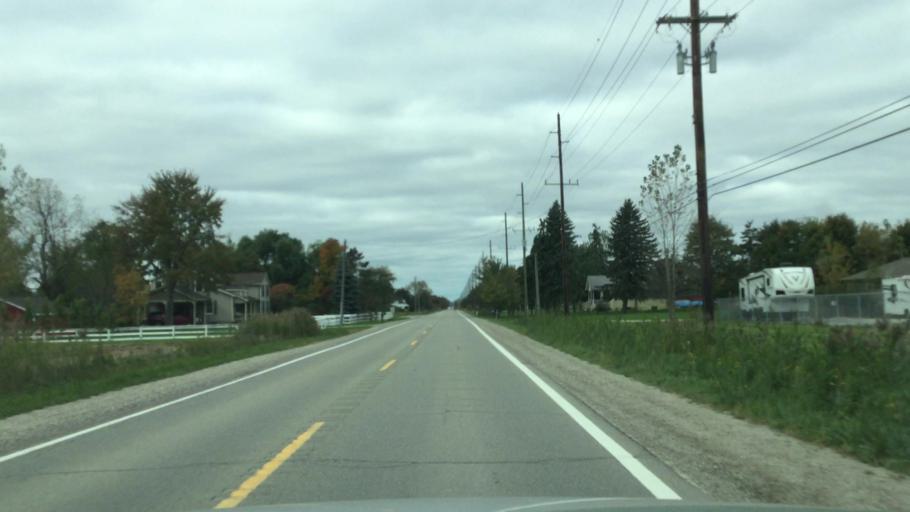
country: US
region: Michigan
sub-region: Macomb County
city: Richmond
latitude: 42.8087
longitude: -82.7786
